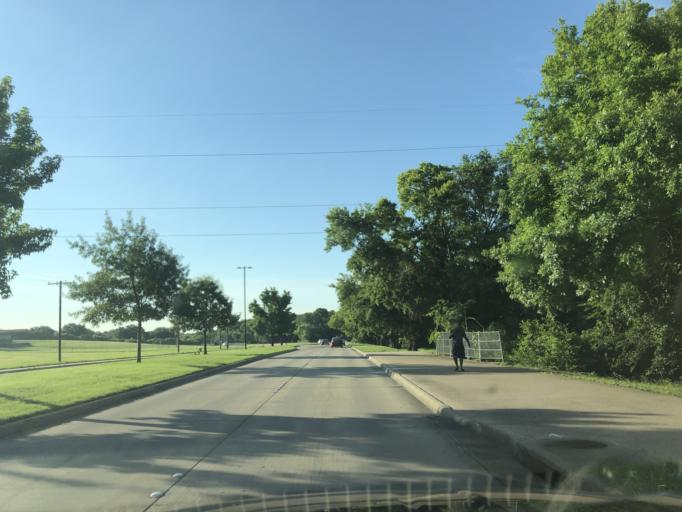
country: US
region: Texas
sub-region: Dallas County
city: Garland
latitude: 32.8502
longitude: -96.6092
